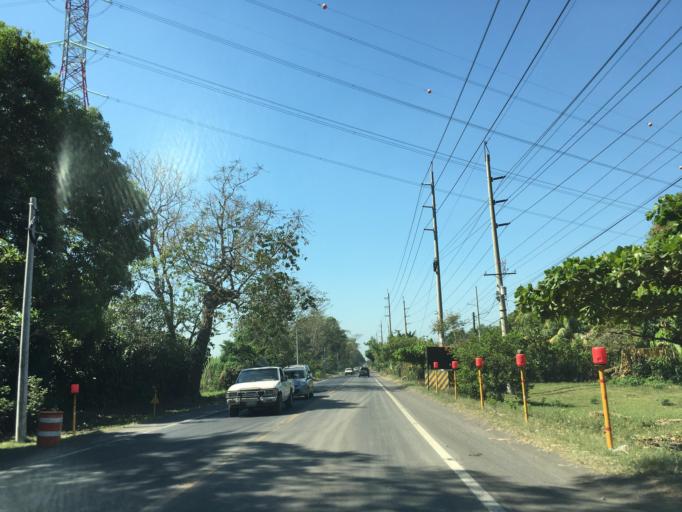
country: GT
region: Escuintla
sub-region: Municipio de Masagua
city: Masagua
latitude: 14.2277
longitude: -90.8264
